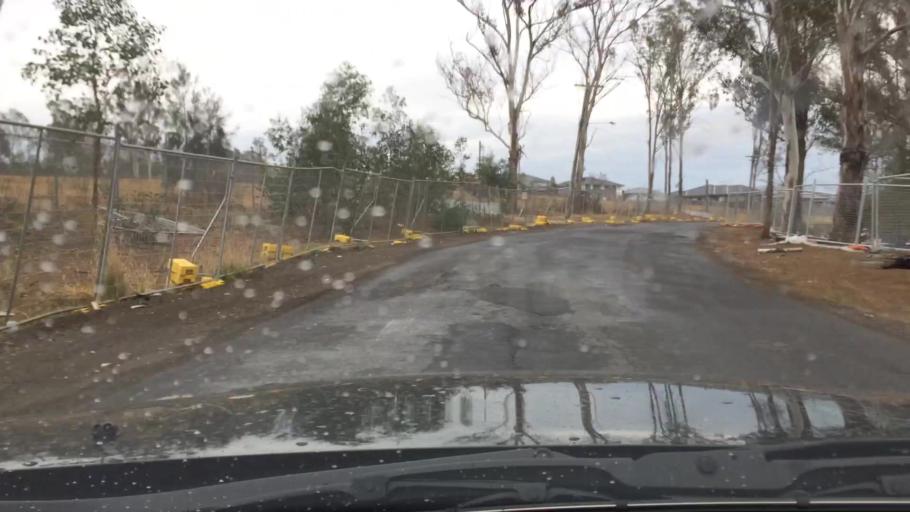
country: AU
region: New South Wales
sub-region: Campbelltown Municipality
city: Denham Court
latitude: -33.9603
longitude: 150.8452
